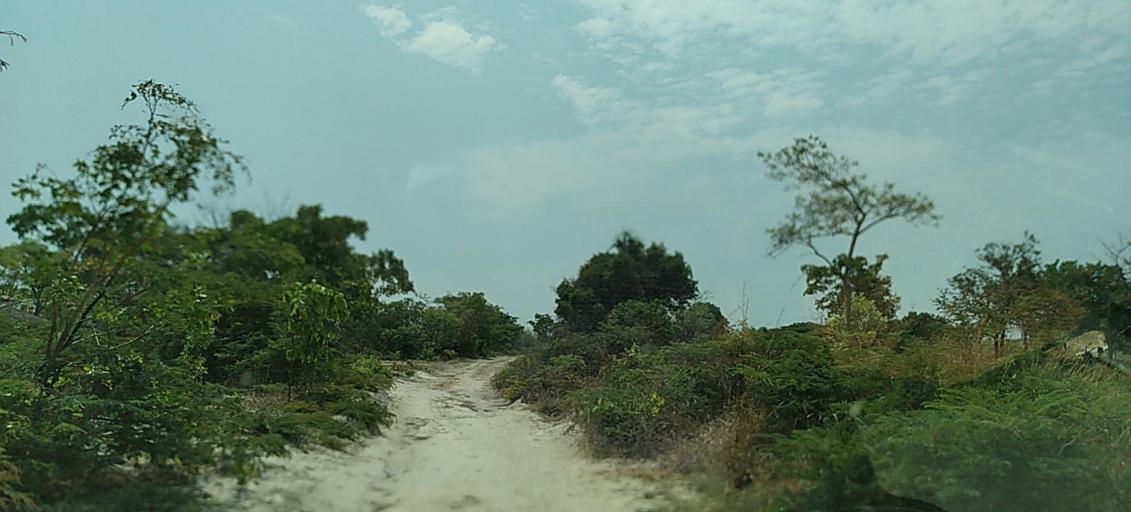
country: ZM
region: Copperbelt
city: Kalulushi
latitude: -12.9419
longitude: 28.1201
